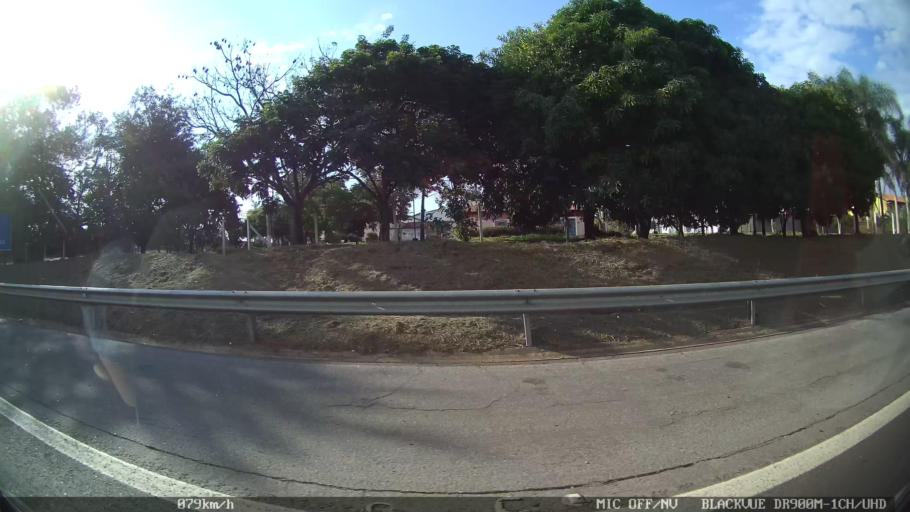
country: BR
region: Sao Paulo
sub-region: Cosmopolis
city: Cosmopolis
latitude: -22.6527
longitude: -47.1875
